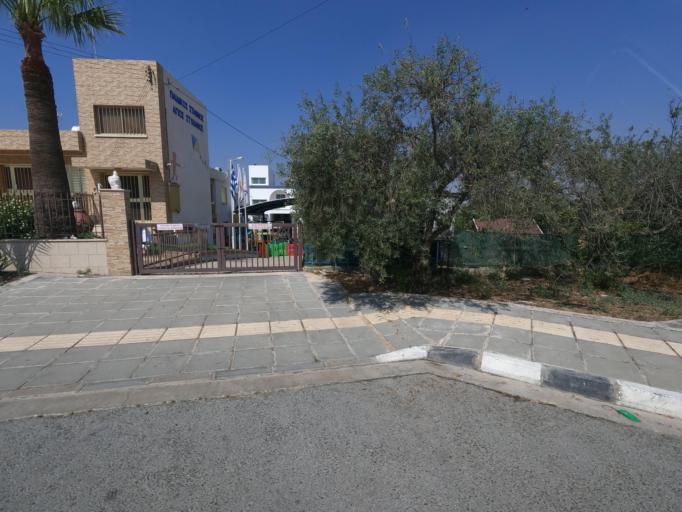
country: CY
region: Lefkosia
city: Lympia
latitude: 34.9975
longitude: 33.4548
